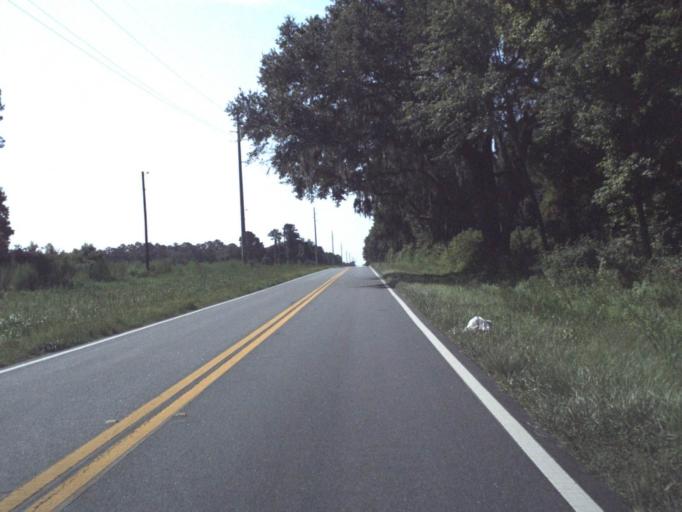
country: US
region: Florida
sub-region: Union County
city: Lake Butler
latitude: 29.9115
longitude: -82.3743
